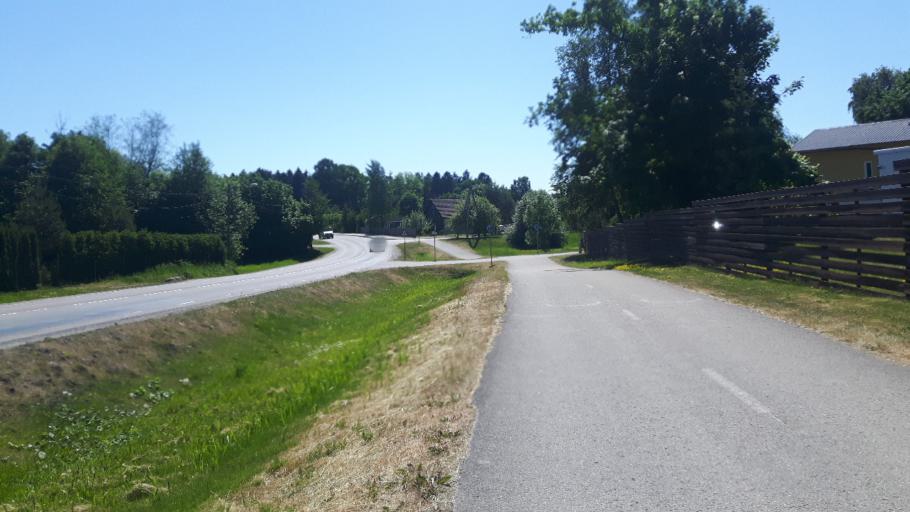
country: EE
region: Harju
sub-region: Saku vald
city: Saku
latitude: 59.2407
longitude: 24.6808
